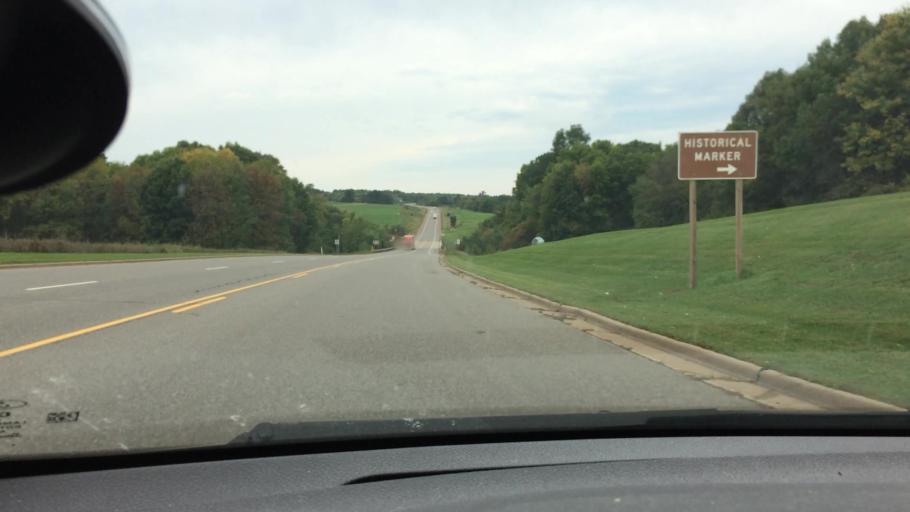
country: US
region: Wisconsin
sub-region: Clark County
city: Neillsville
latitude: 44.5523
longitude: -90.6043
